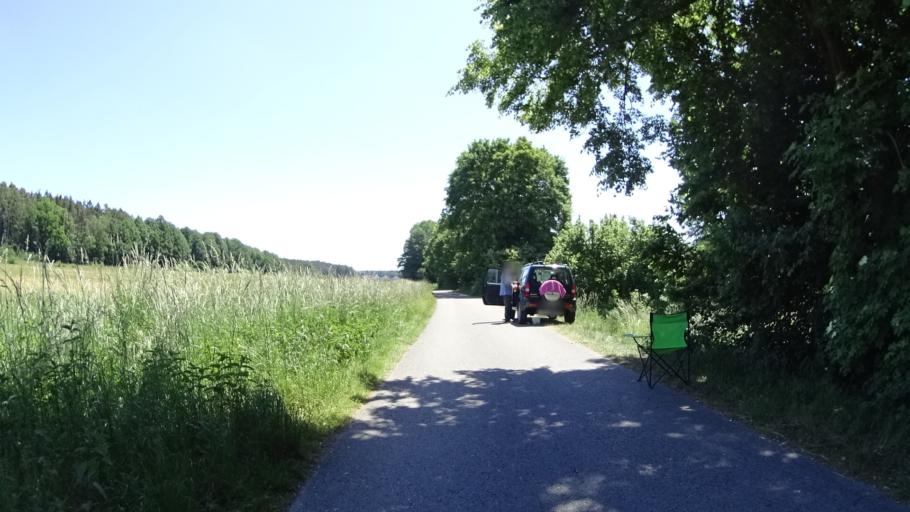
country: DE
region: Bavaria
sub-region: Regierungsbezirk Mittelfranken
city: Pleinfeld
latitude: 49.1089
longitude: 10.9405
